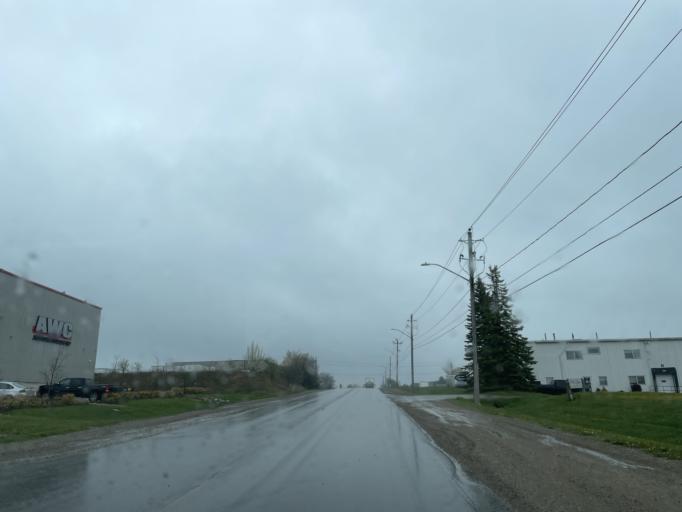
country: CA
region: Ontario
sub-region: Wellington County
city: Guelph
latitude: 43.5499
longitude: -80.3055
